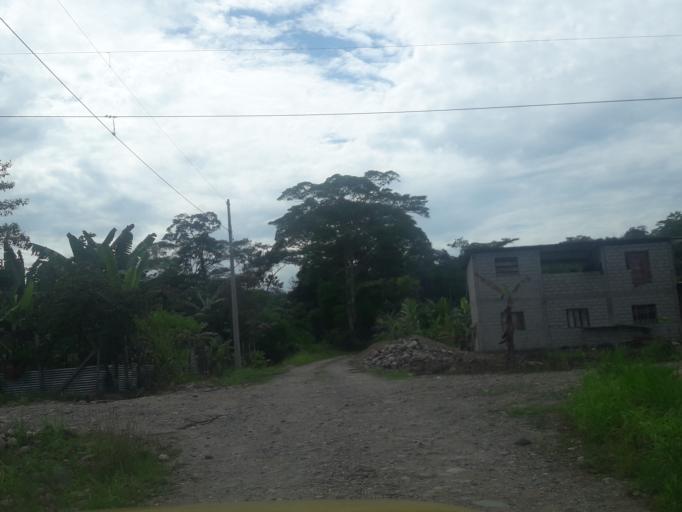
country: EC
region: Napo
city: Tena
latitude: -1.0576
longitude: -77.7937
